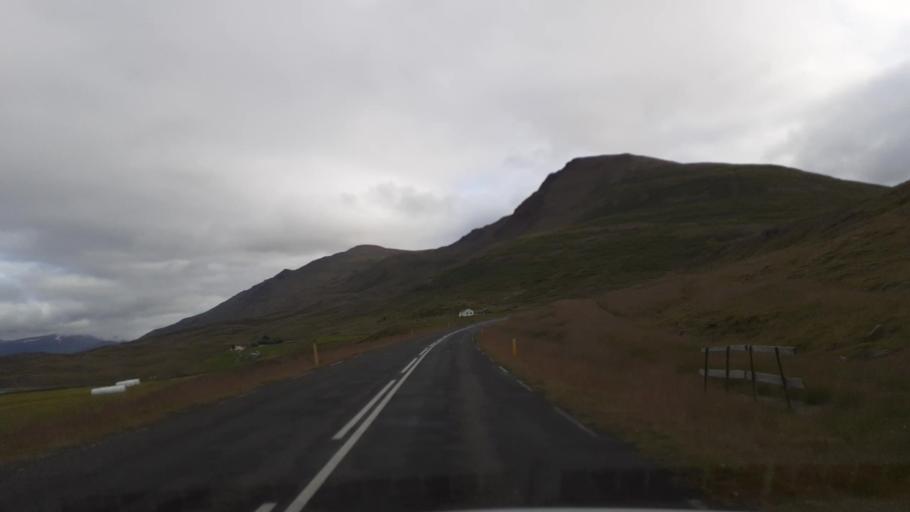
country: IS
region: Northeast
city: Akureyri
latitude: 65.8111
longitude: -18.0535
